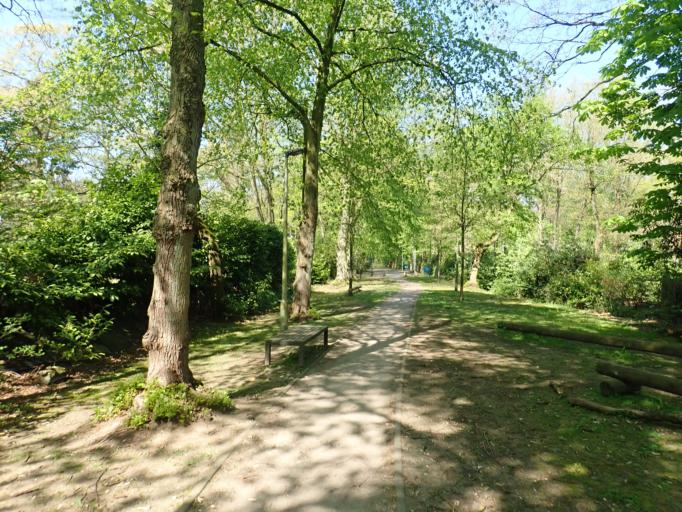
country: BE
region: Flanders
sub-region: Provincie Antwerpen
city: Brasschaat
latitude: 51.3243
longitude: 4.5167
